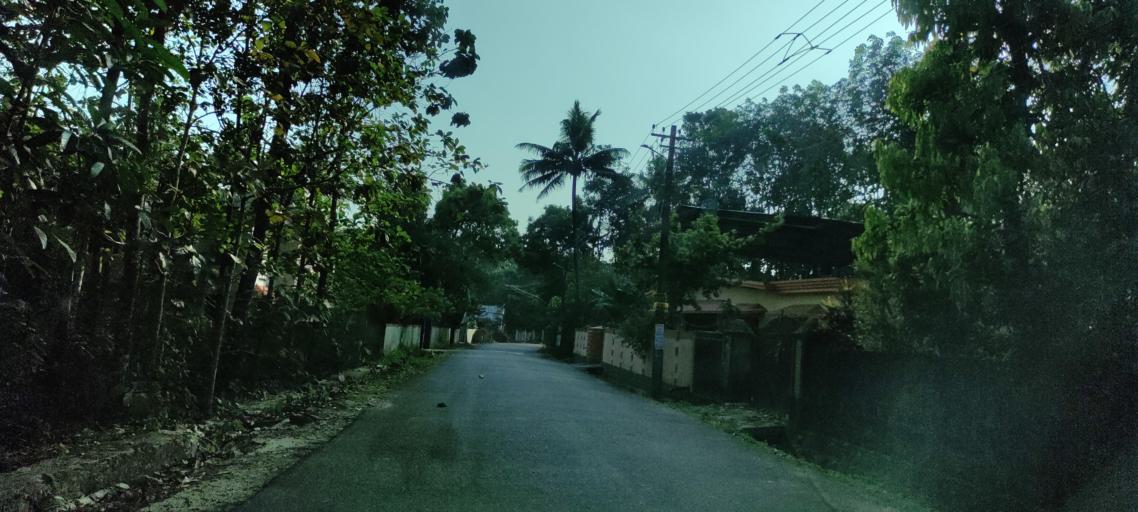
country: IN
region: Kerala
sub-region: Pattanamtitta
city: Adur
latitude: 9.1449
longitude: 76.7452
